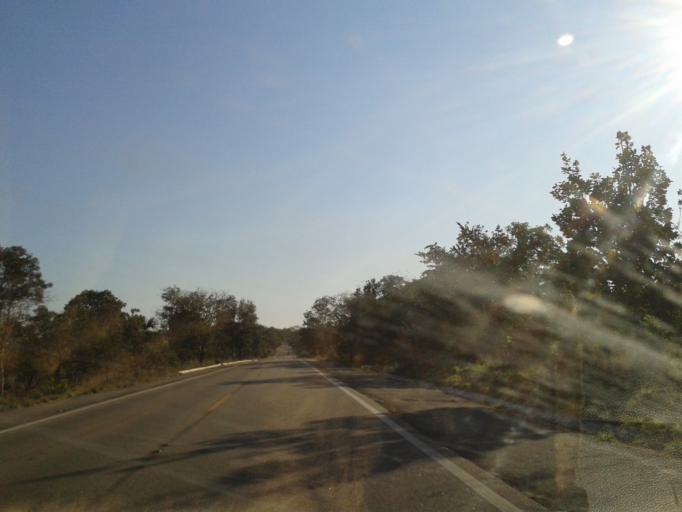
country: BR
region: Goias
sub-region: Itapuranga
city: Itapuranga
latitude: -15.3813
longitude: -50.3892
